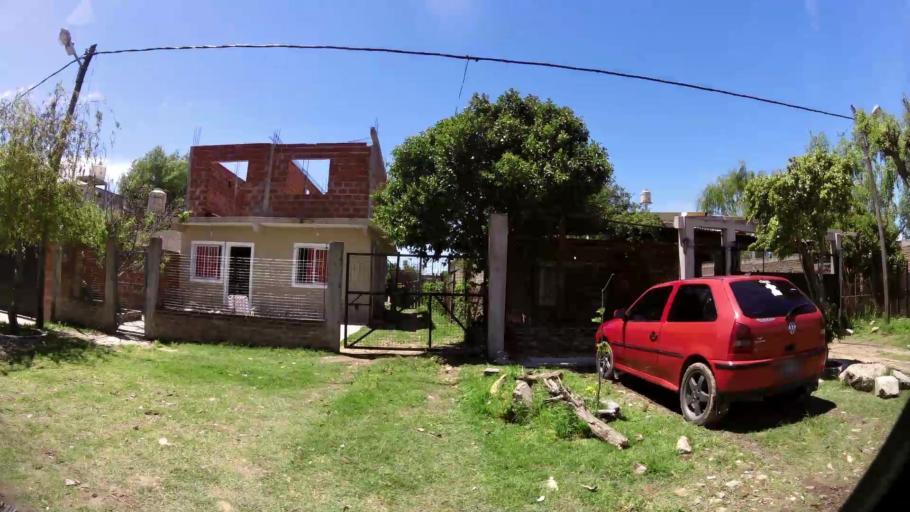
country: AR
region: Buenos Aires
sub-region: Partido de Quilmes
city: Quilmes
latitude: -34.7398
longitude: -58.3083
